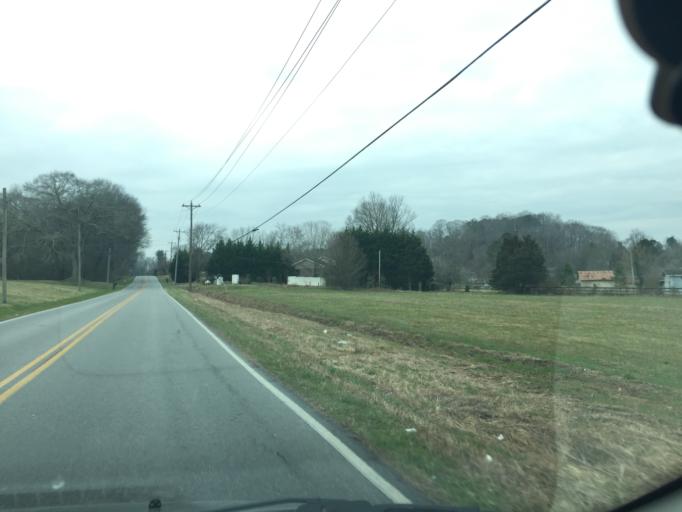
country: US
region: Tennessee
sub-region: Hamilton County
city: East Brainerd
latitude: 34.9760
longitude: -85.1476
